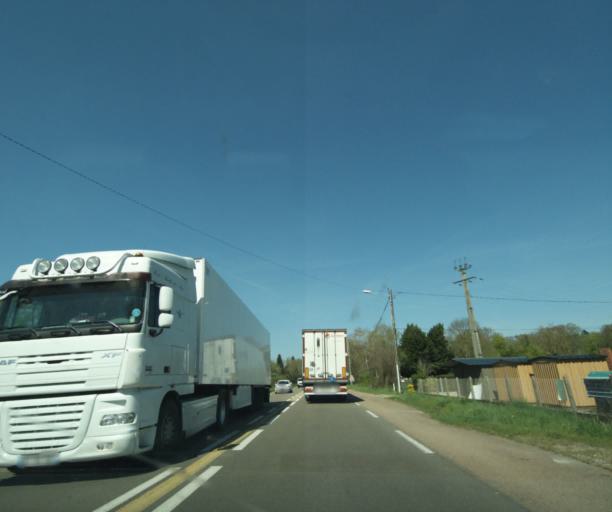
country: FR
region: Bourgogne
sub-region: Departement de la Nievre
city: Chantenay-Saint-Imbert
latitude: 46.7256
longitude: 3.1765
